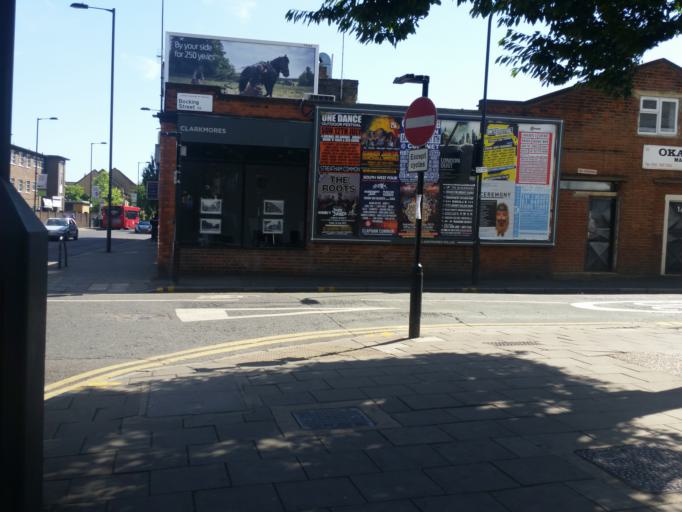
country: GB
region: England
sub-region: Greater London
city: Bethnal Green
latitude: 51.5375
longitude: -0.0570
